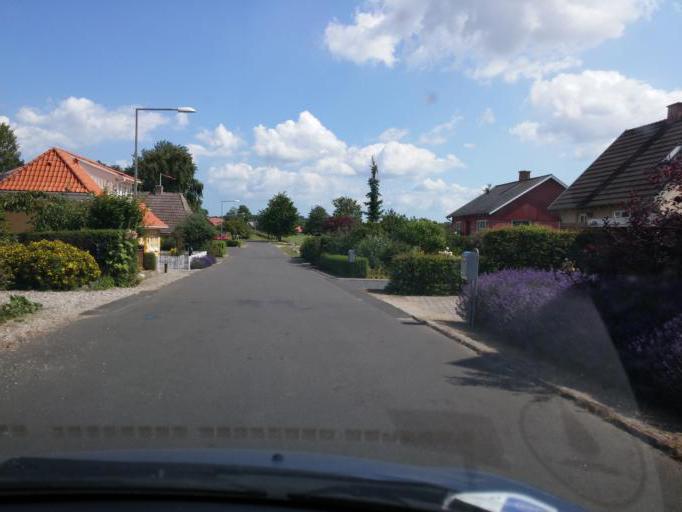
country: DK
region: South Denmark
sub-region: Kerteminde Kommune
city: Munkebo
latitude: 55.4529
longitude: 10.5516
